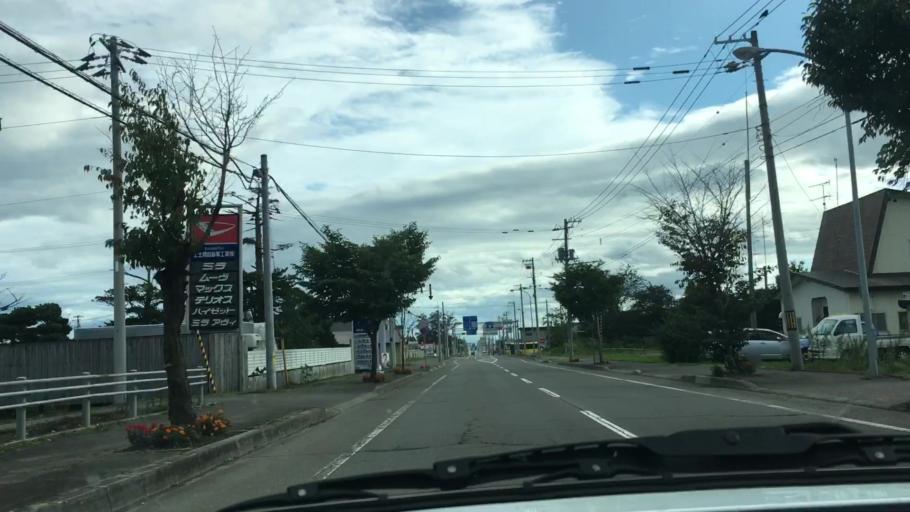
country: JP
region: Hokkaido
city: Otofuke
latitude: 43.2364
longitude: 143.2959
